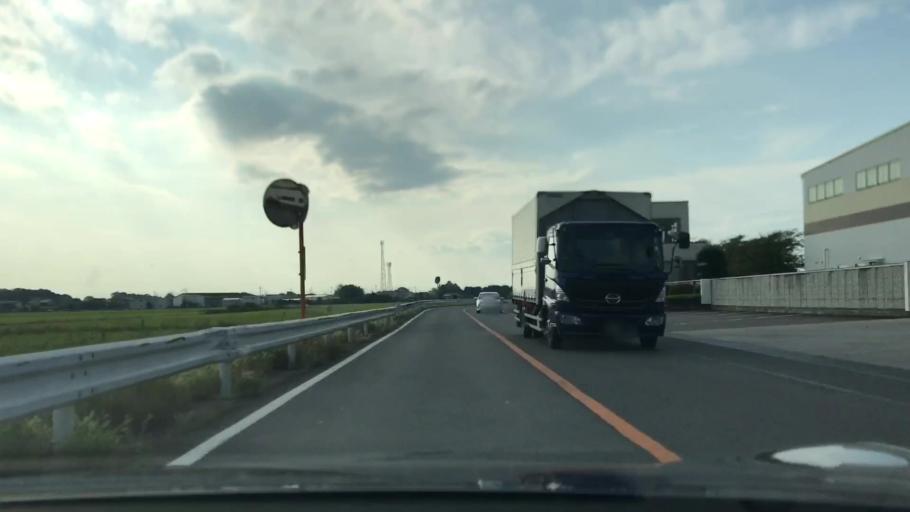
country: JP
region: Saitama
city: Menuma
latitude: 36.2111
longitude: 139.4520
